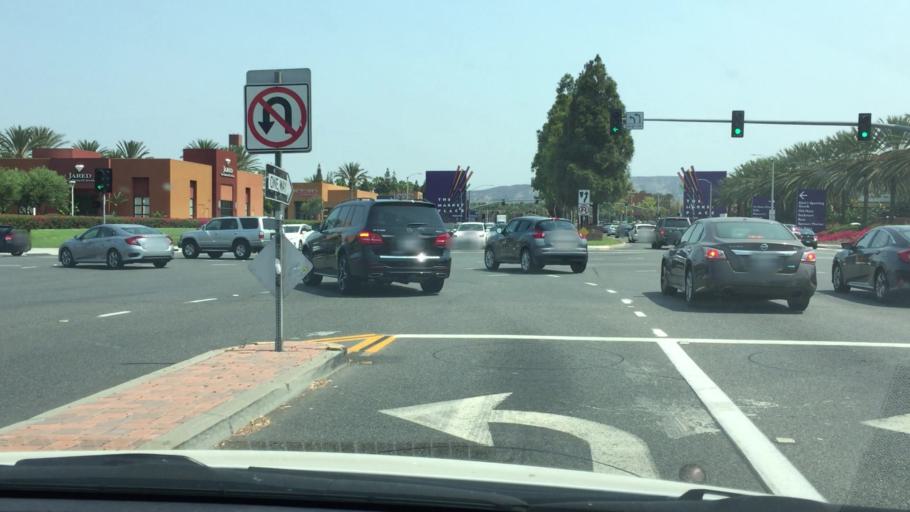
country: US
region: California
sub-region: Orange County
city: Tustin
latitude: 33.7222
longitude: -117.7926
